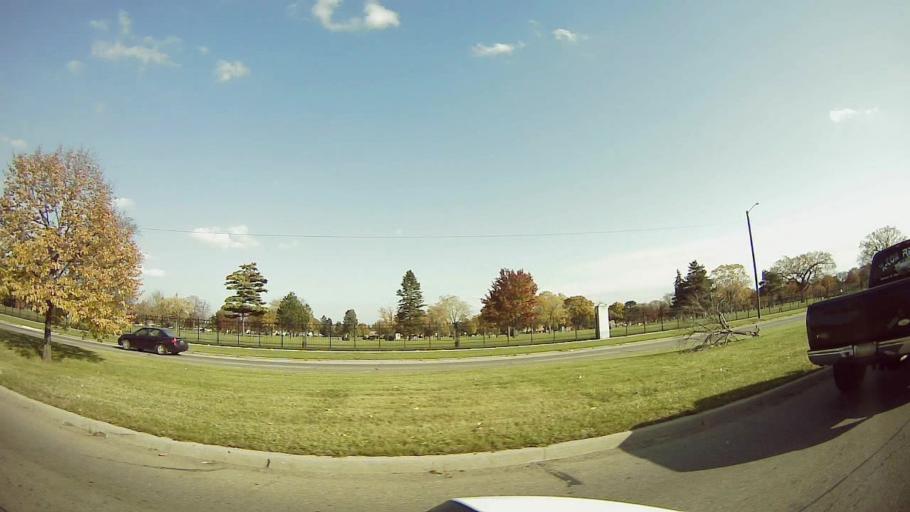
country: US
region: Michigan
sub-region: Wayne County
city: Hamtramck
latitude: 42.4247
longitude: -83.0141
